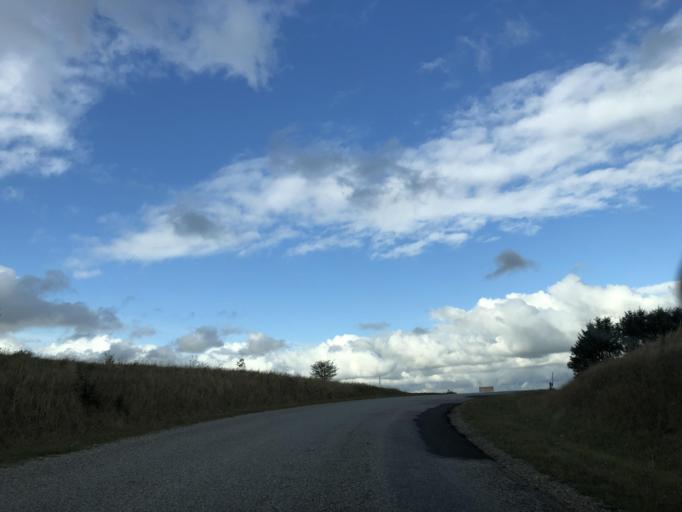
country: DK
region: South Denmark
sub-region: Varde Kommune
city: Olgod
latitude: 55.7650
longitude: 8.6220
